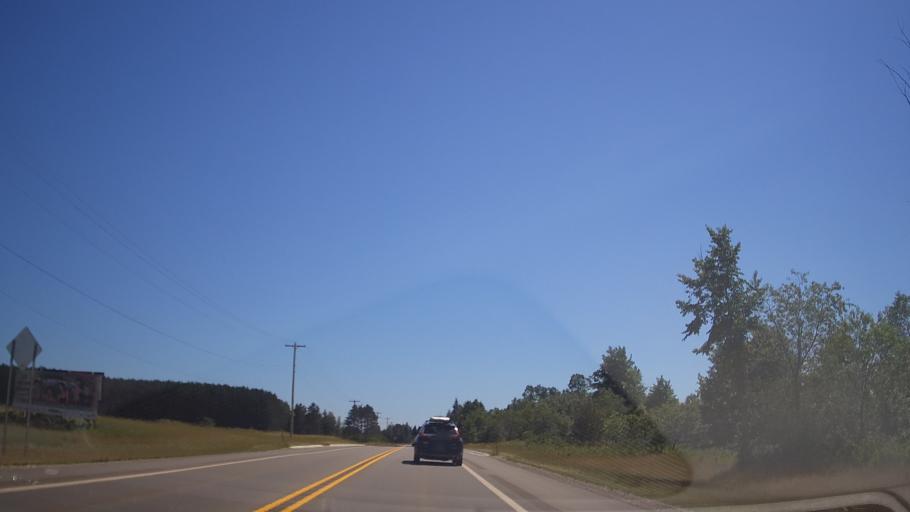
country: US
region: Michigan
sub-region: Mackinac County
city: Saint Ignace
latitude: 45.6153
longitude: -84.7803
